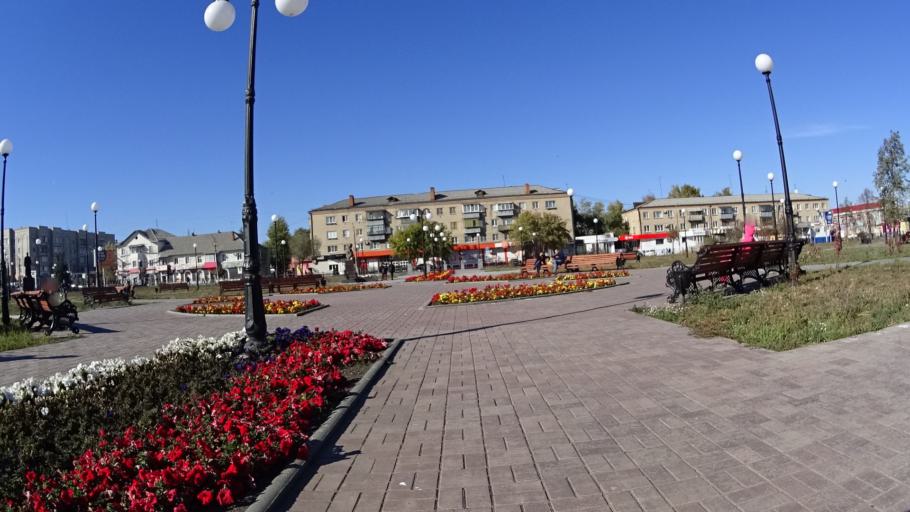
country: RU
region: Chelyabinsk
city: Troitsk
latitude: 54.0873
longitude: 61.5580
